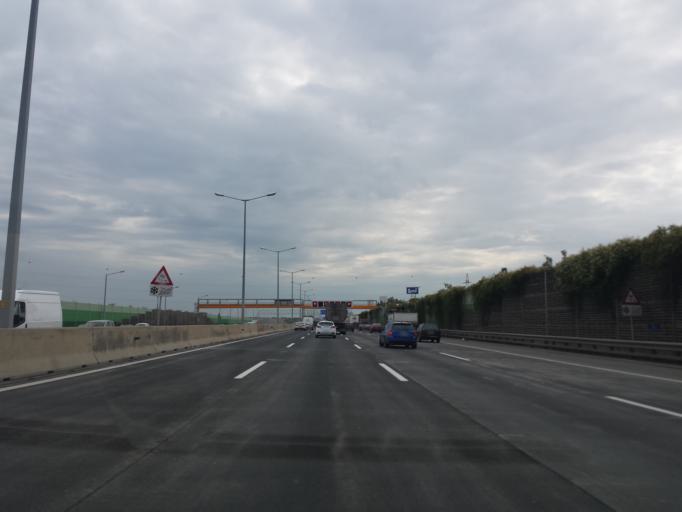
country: AT
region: Lower Austria
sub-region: Politischer Bezirk Modling
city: Vosendorf
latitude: 48.1311
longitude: 16.3296
